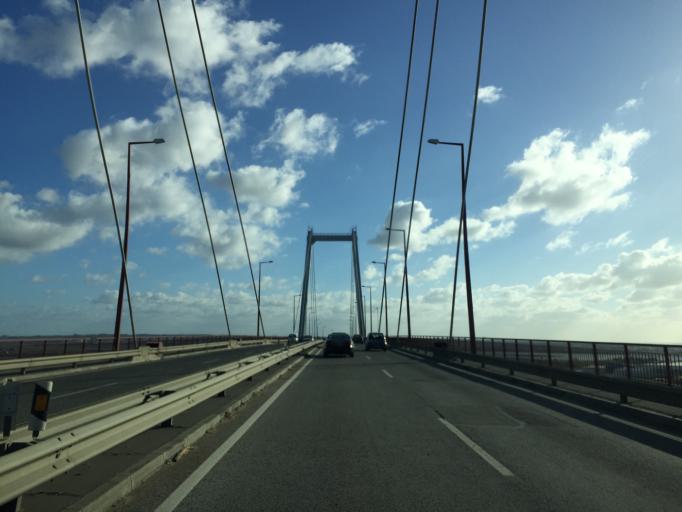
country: PT
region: Coimbra
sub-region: Figueira da Foz
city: Figueira da Foz
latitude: 40.1464
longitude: -8.8419
